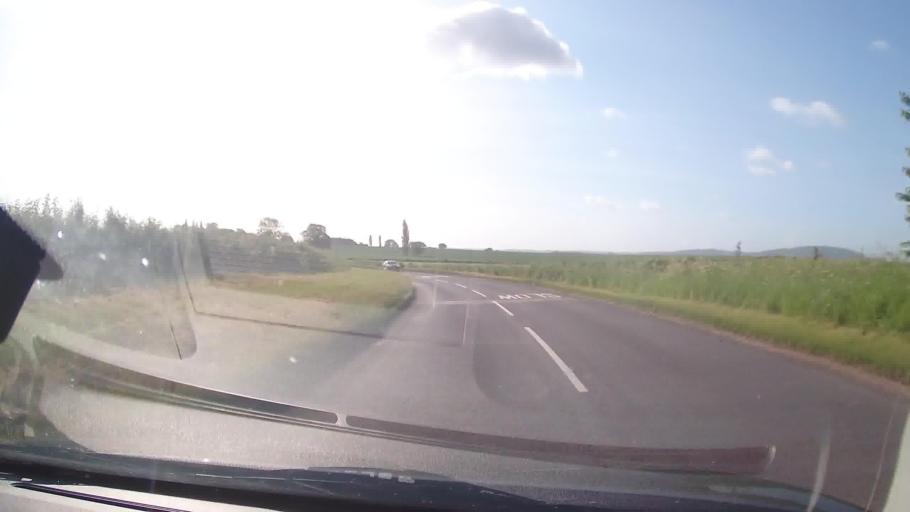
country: GB
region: England
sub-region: Shropshire
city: Withington
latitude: 52.7537
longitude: -2.6003
